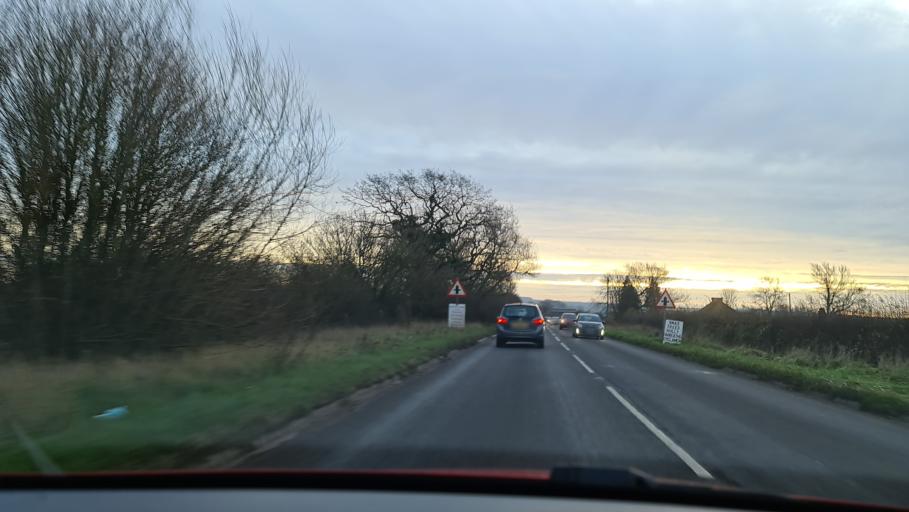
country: GB
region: England
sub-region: Buckinghamshire
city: Princes Risborough
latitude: 51.7501
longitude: -0.8780
